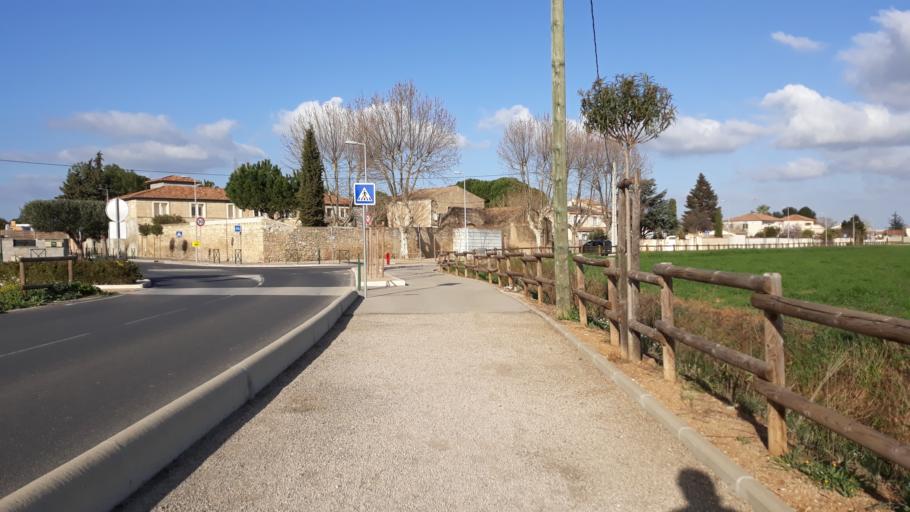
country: FR
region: Languedoc-Roussillon
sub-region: Departement du Gard
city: Aimargues
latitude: 43.6896
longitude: 4.2013
